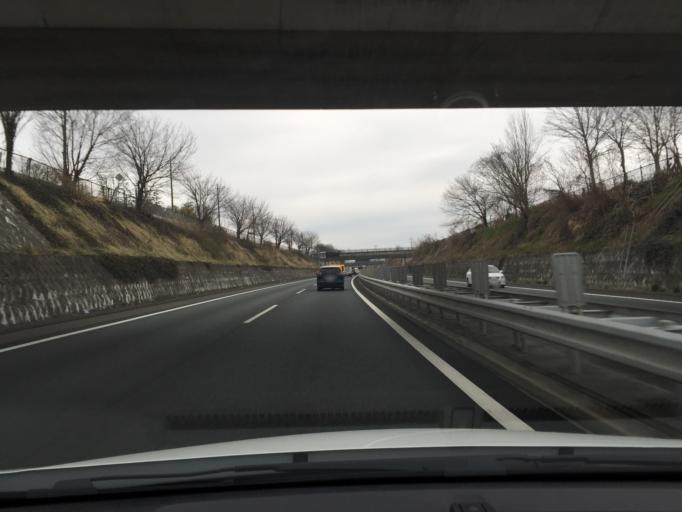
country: JP
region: Saitama
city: Hanno
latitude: 35.8071
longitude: 139.3490
